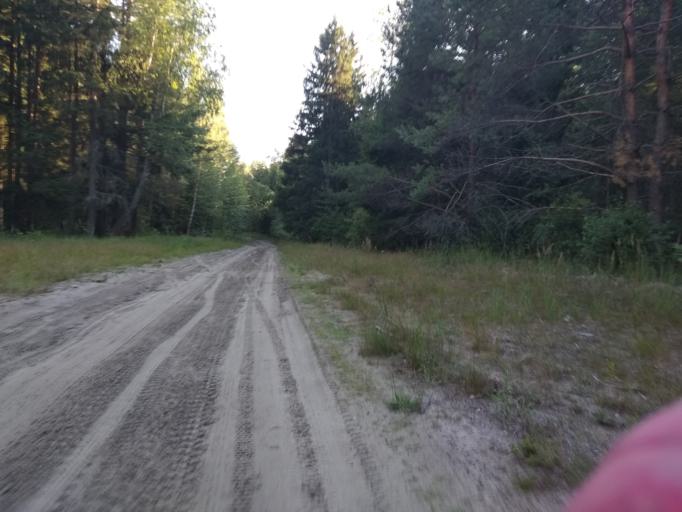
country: RU
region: Moskovskaya
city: Misheronskiy
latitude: 55.7317
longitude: 39.7644
